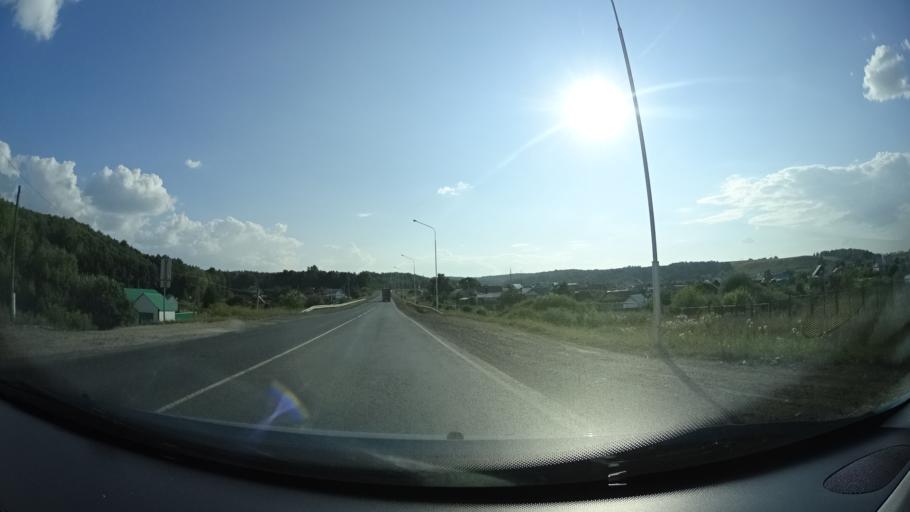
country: RU
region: Tatarstan
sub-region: Bavlinskiy Rayon
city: Bavly
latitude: 54.4600
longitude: 53.2825
